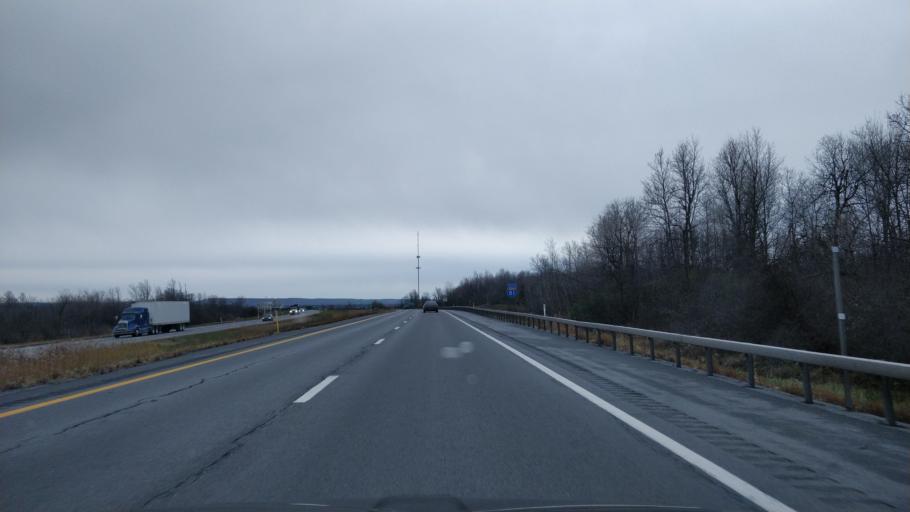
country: US
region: New York
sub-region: Jefferson County
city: Watertown
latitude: 44.0298
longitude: -75.9163
